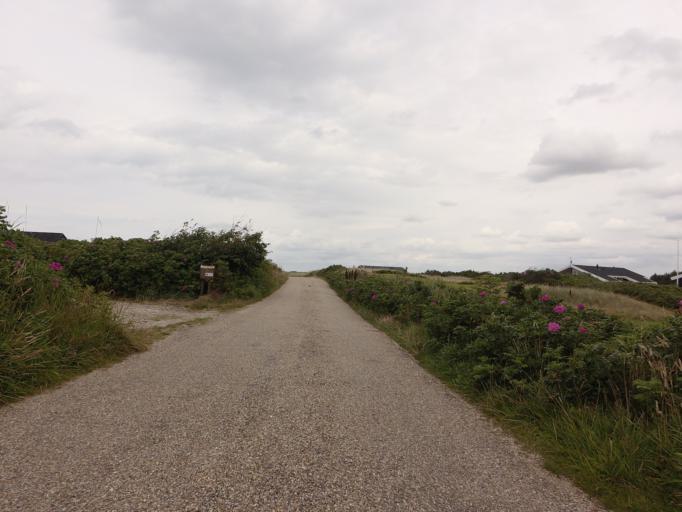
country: DK
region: North Denmark
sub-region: Jammerbugt Kommune
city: Pandrup
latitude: 57.3101
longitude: 9.6524
